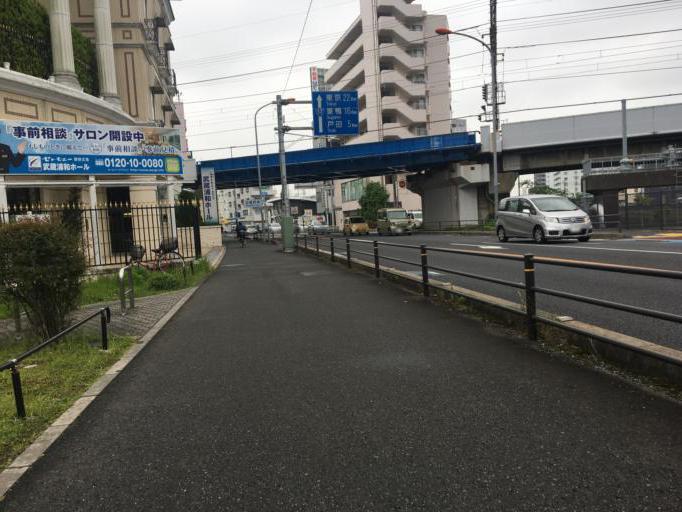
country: JP
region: Saitama
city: Yono
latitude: 35.8462
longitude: 139.6510
